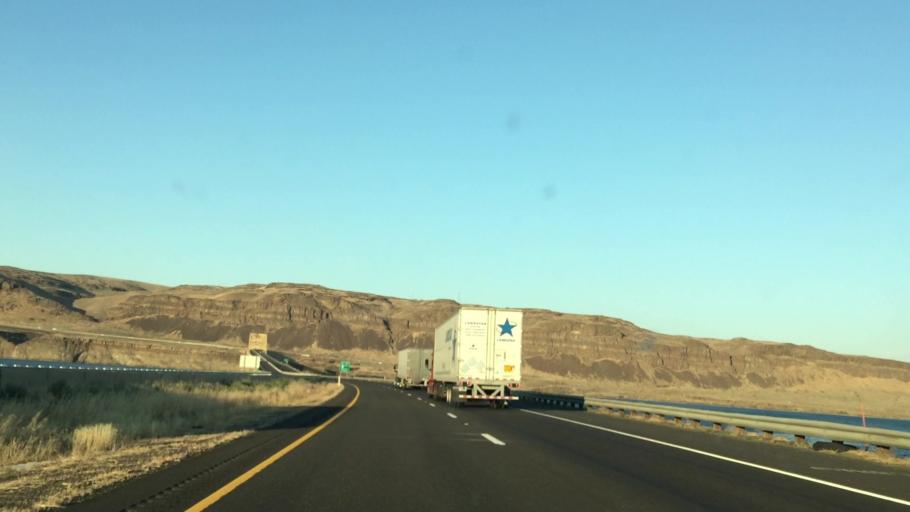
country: US
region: Washington
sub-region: Grant County
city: Mattawa
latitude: 46.9402
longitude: -119.9790
